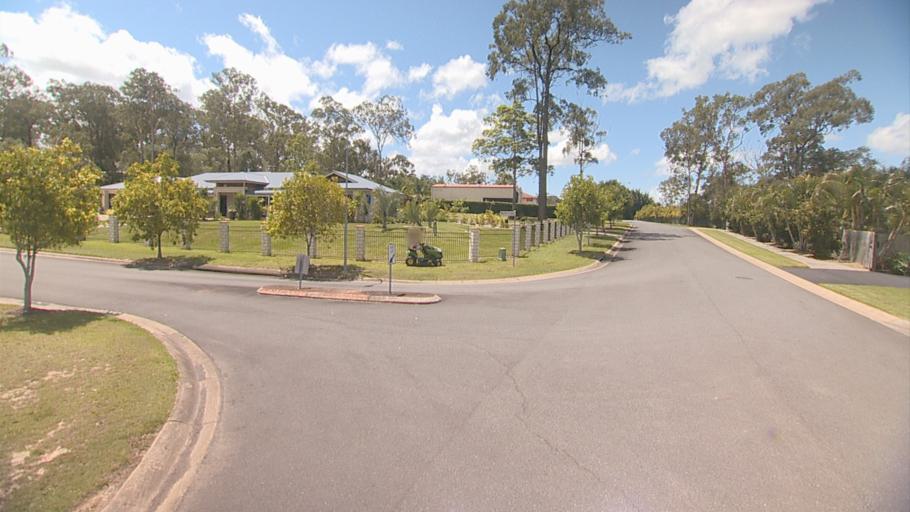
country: AU
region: Queensland
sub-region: Gold Coast
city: Yatala
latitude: -27.6684
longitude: 153.2301
